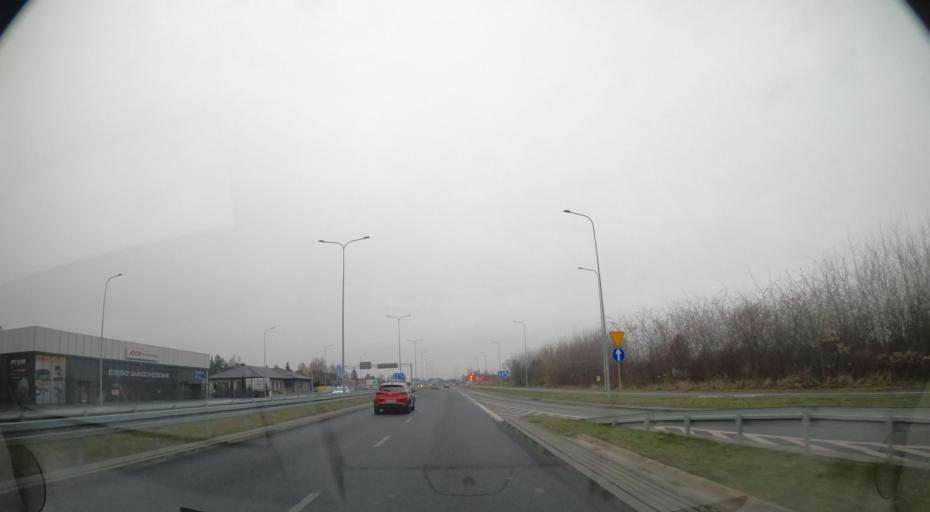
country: PL
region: Masovian Voivodeship
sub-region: Radom
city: Radom
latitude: 51.3947
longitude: 21.1959
